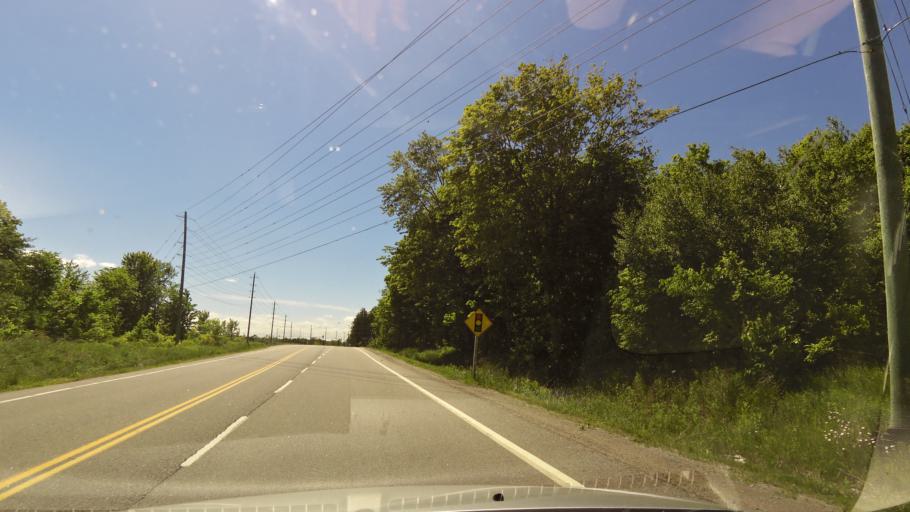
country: CA
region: Ontario
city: Vaughan
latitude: 43.9476
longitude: -79.5300
